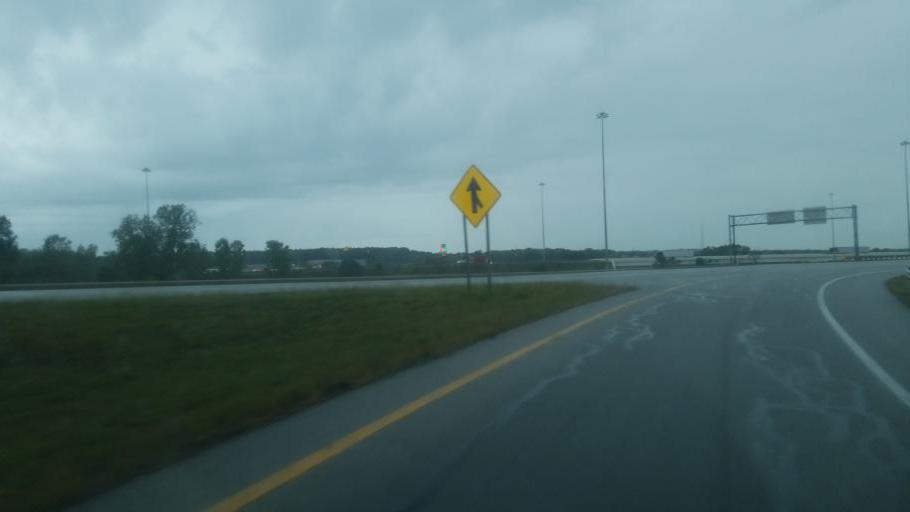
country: US
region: Ohio
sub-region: Medina County
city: Westfield Center
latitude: 41.0287
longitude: -81.8983
